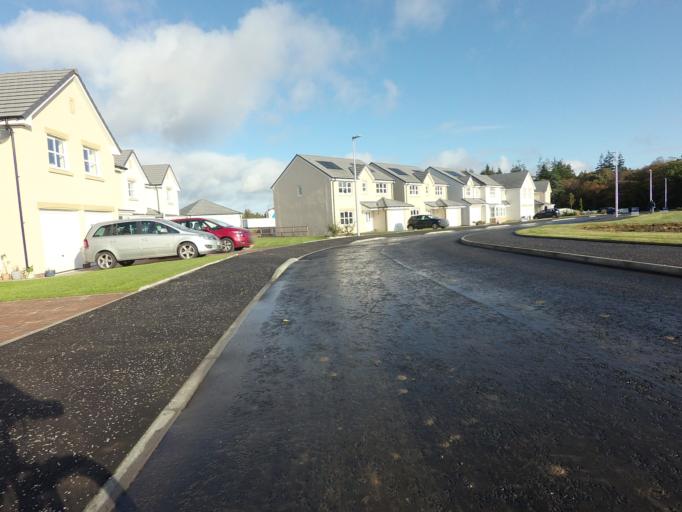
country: GB
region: Scotland
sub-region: West Lothian
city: West Calder
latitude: 55.8674
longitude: -3.5365
